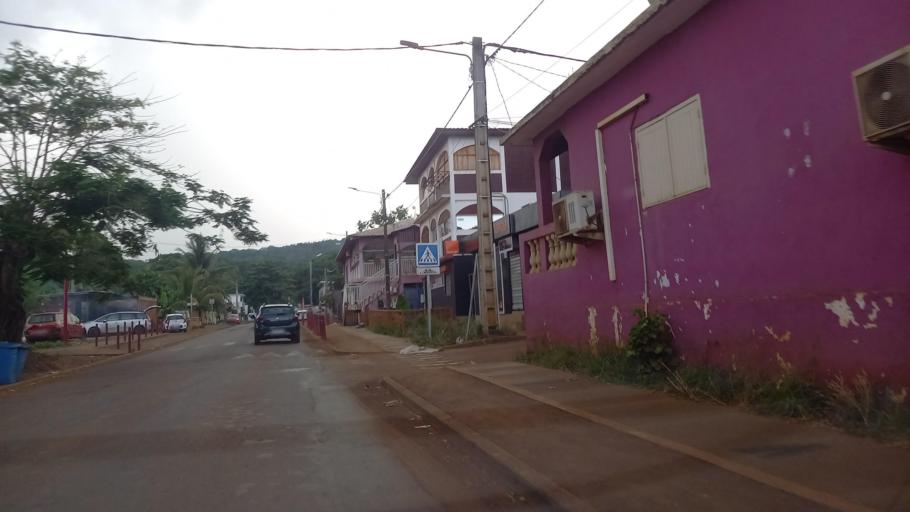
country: YT
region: Dembeni
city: Dembeni
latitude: -12.8376
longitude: 45.1745
